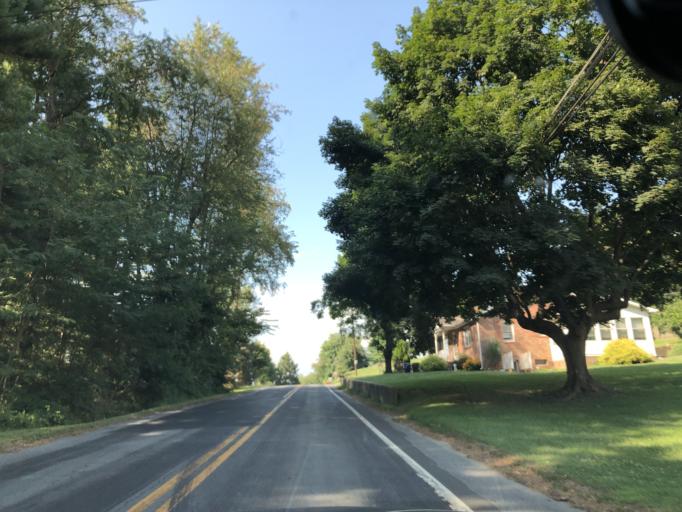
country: US
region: Maryland
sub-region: Frederick County
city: Linganore
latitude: 39.4719
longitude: -77.1865
